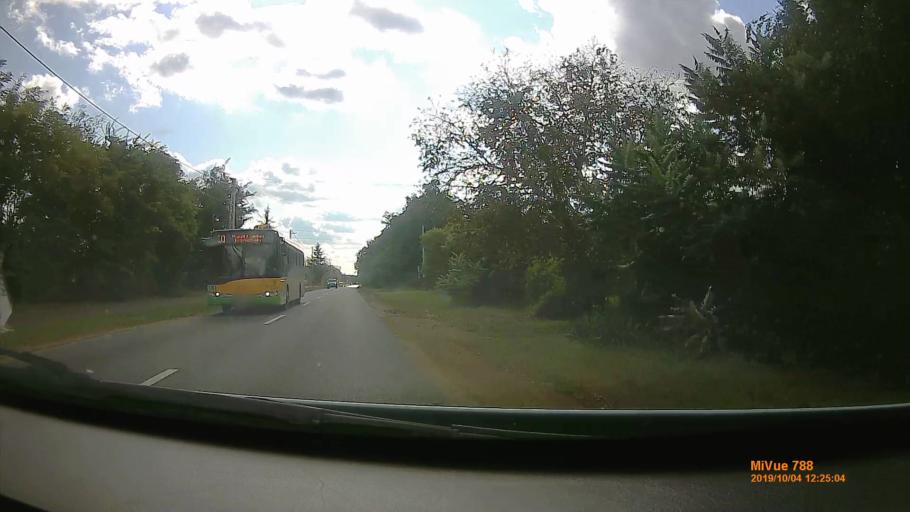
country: HU
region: Szabolcs-Szatmar-Bereg
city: Nyiregyhaza
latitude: 47.9900
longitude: 21.7040
